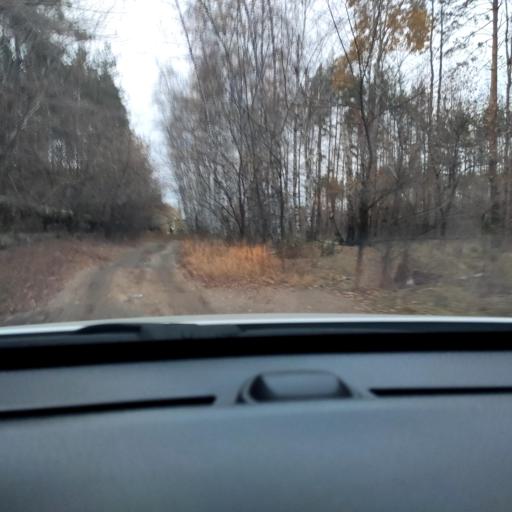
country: RU
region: Voronezj
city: Somovo
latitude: 51.6835
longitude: 39.2851
